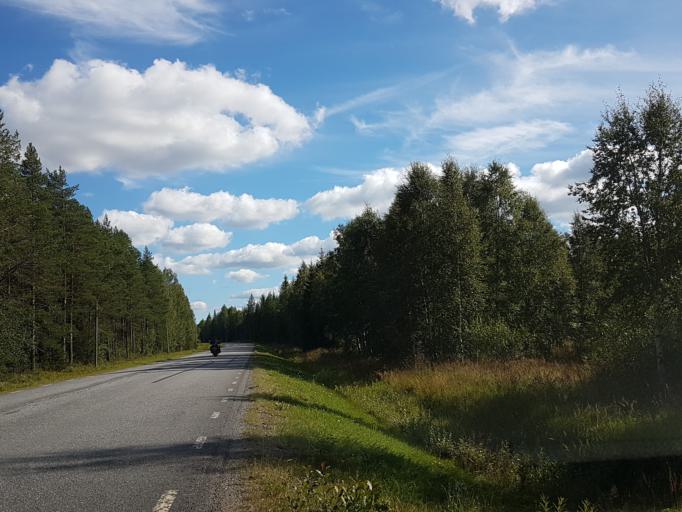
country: SE
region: Vaesterbotten
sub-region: Skelleftea Kommun
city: Burtraesk
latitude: 64.3282
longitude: 20.5256
